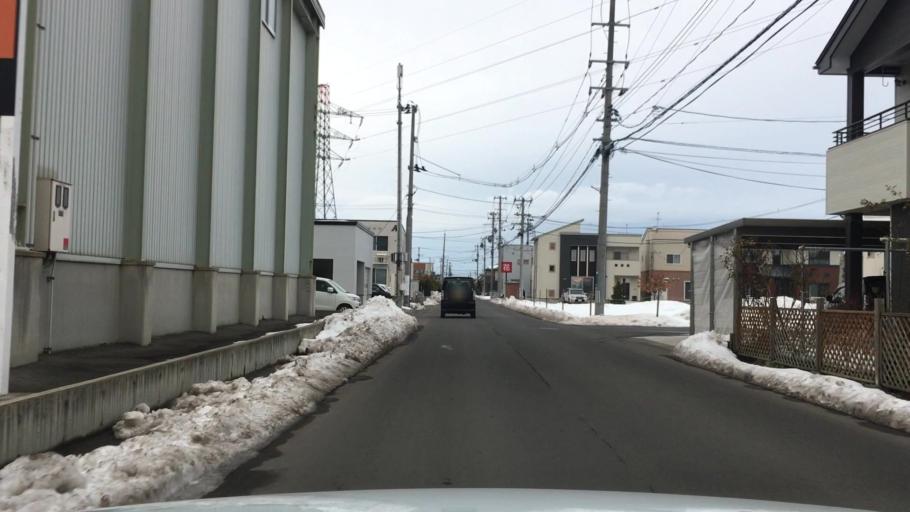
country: JP
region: Aomori
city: Hirosaki
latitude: 40.5994
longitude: 140.5093
